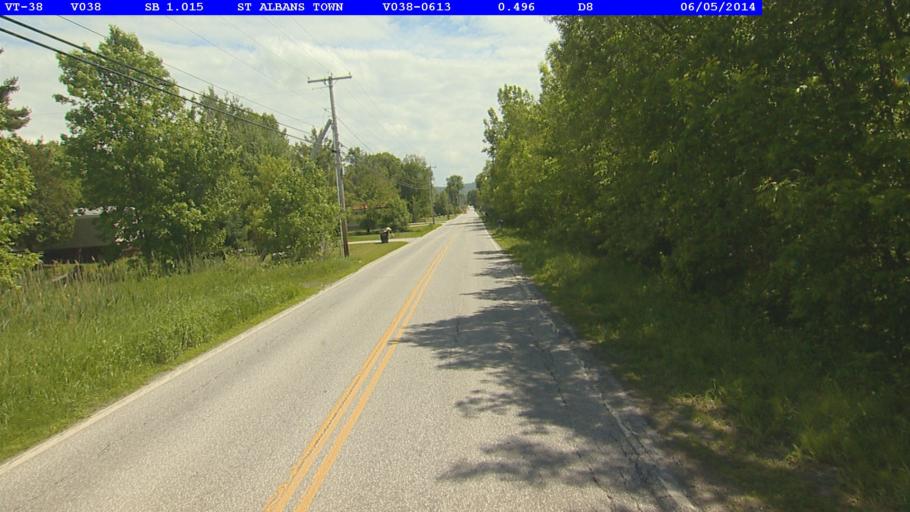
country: US
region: Vermont
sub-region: Franklin County
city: Saint Albans
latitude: 44.8305
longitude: -73.0932
